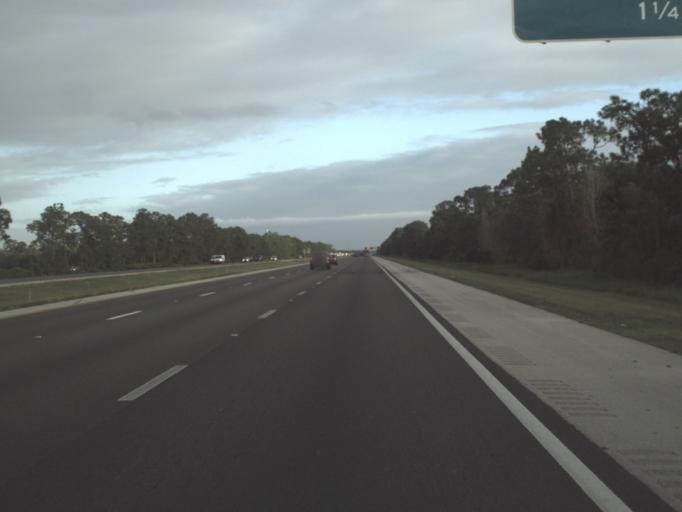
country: US
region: Florida
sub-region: Lee County
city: Three Oaks
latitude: 26.4573
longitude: -81.7864
